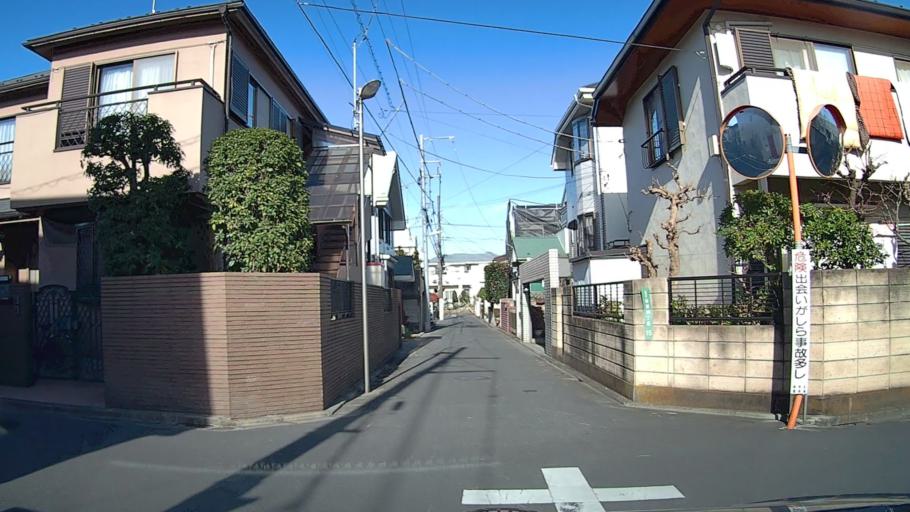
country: JP
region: Saitama
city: Wako
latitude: 35.7549
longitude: 139.6132
